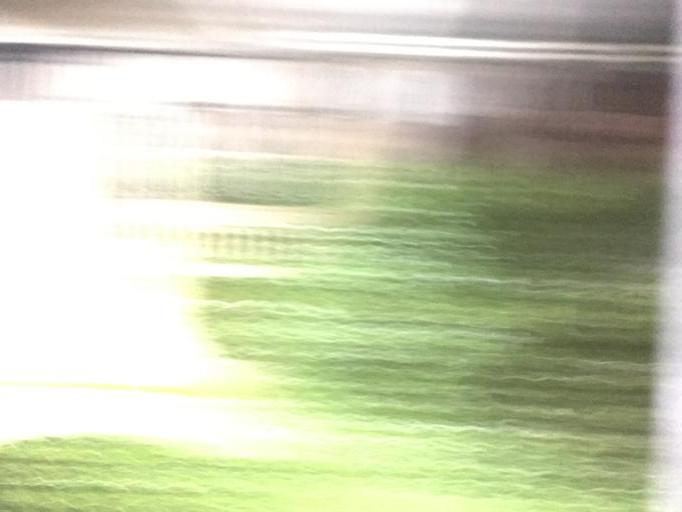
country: AR
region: Buenos Aires
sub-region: Partido de Lanus
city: Lanus
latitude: -34.6815
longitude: -58.4186
